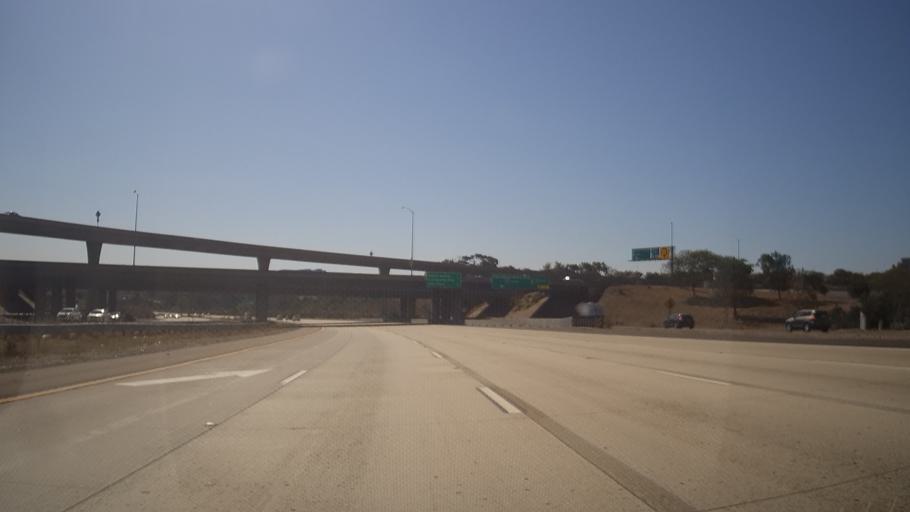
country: US
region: California
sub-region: San Diego County
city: La Mesa
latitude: 32.8434
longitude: -117.1210
